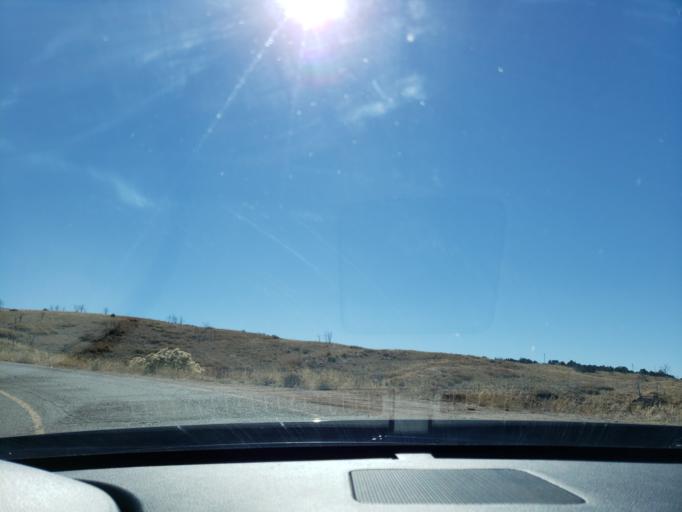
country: US
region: Colorado
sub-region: Fremont County
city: Canon City
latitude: 38.4703
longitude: -105.3099
